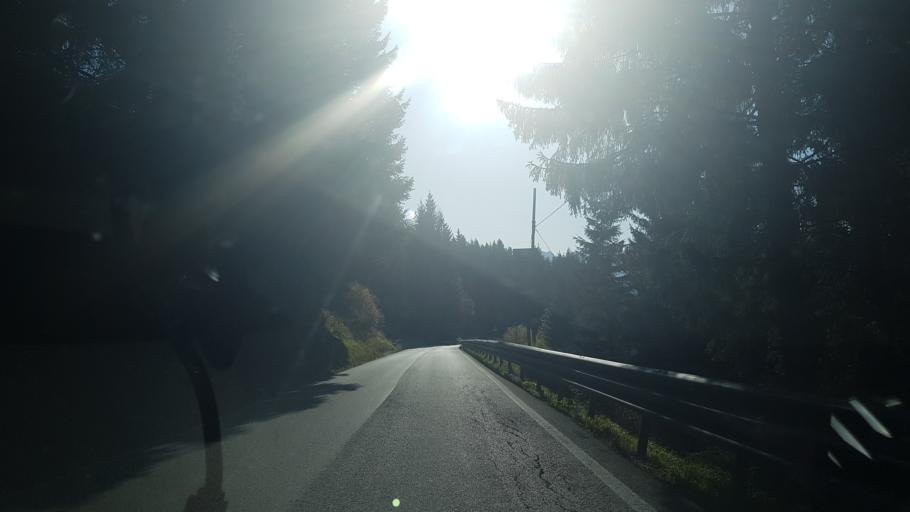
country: IT
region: Veneto
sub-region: Provincia di Belluno
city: Candide
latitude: 46.6249
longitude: 12.4692
